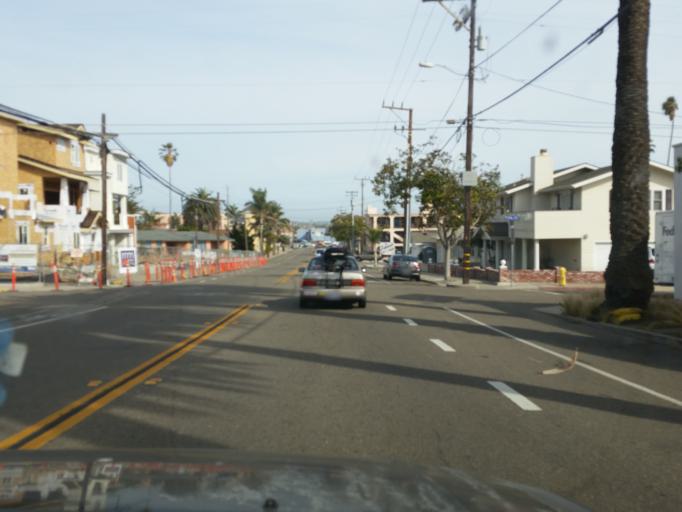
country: US
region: California
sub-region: San Luis Obispo County
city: Pismo Beach
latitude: 35.1438
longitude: -120.6444
